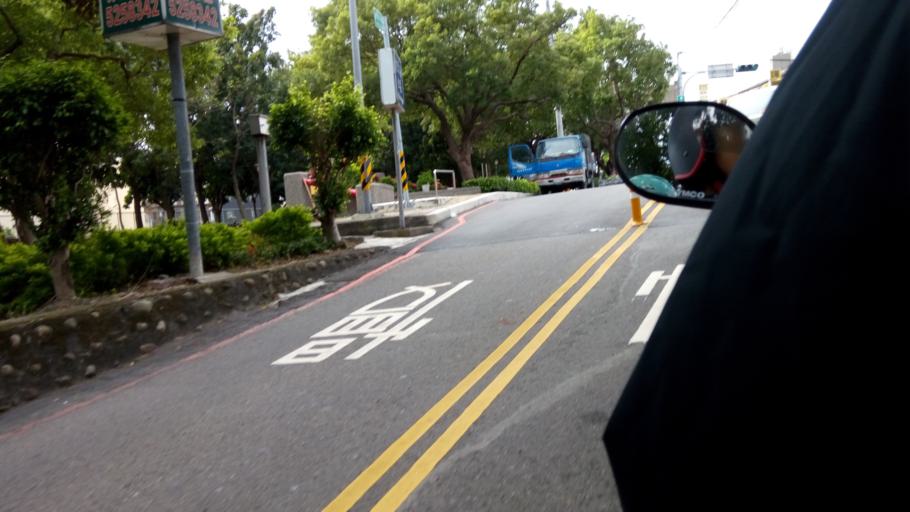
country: TW
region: Taiwan
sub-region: Hsinchu
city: Hsinchu
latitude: 24.7967
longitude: 120.9584
